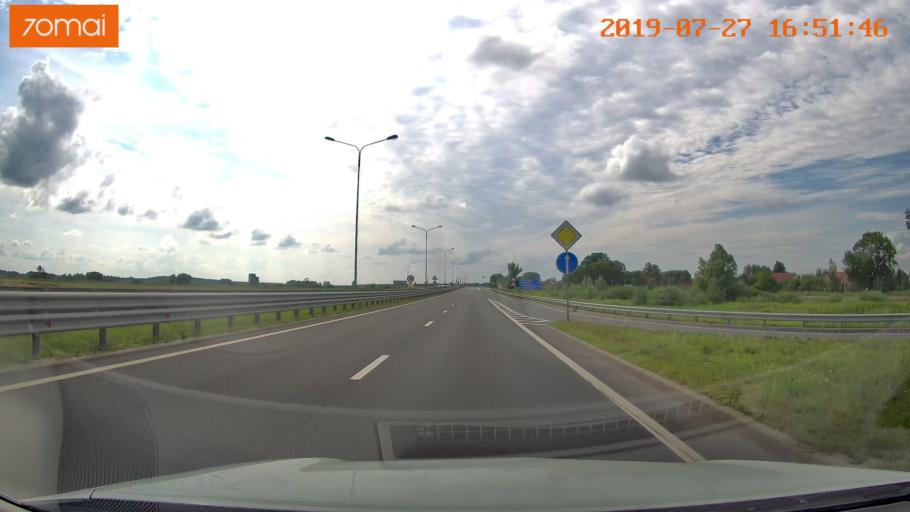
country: RU
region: Kaliningrad
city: Gvardeysk
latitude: 54.6836
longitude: 20.8781
